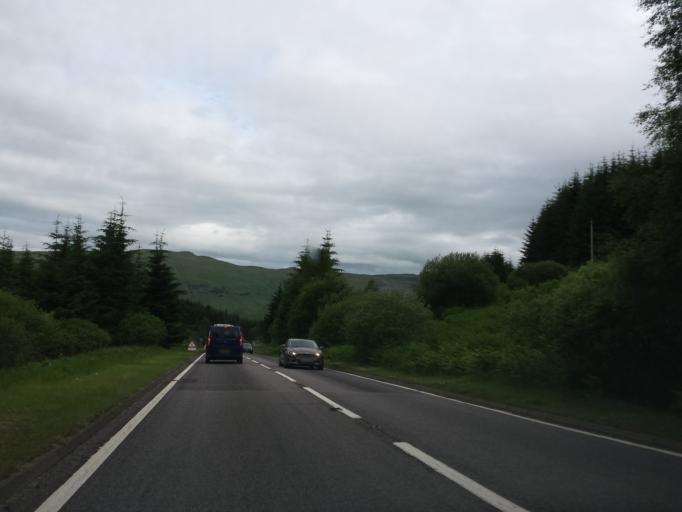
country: GB
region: Scotland
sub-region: Stirling
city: Callander
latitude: 56.4299
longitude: -4.3402
